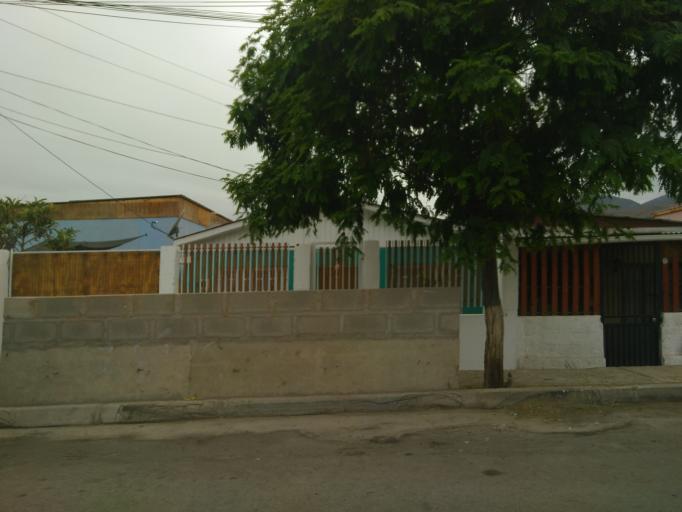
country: CL
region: Antofagasta
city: Taltal
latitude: -25.4046
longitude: -70.4785
